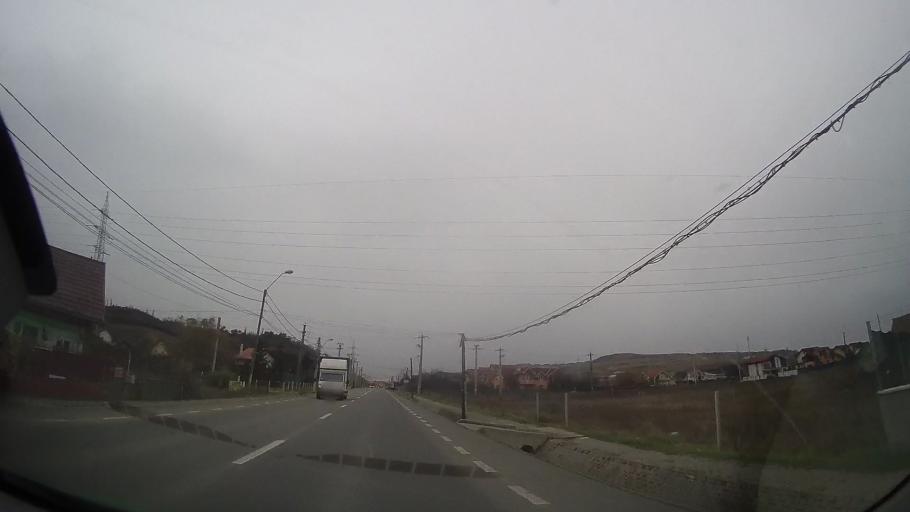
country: RO
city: Remetea
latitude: 46.5930
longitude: 24.5339
